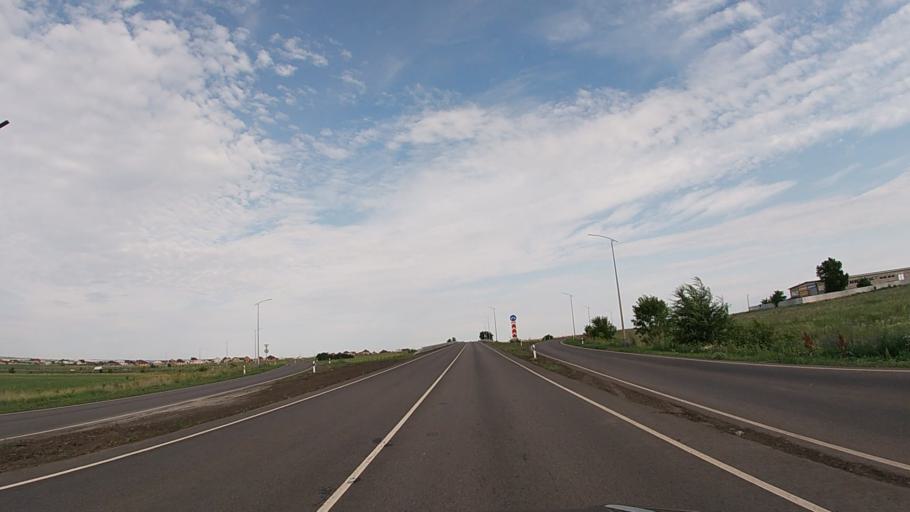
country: RU
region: Belgorod
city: Severnyy
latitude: 50.6731
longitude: 36.4776
